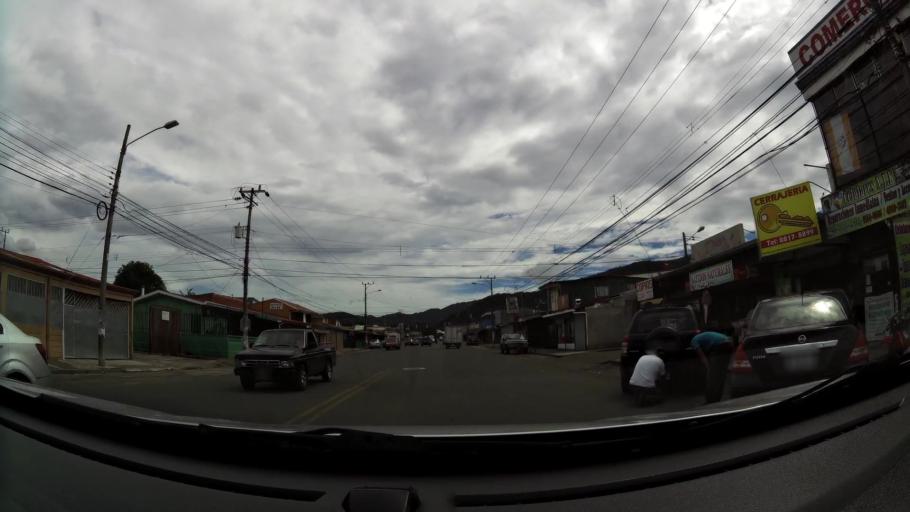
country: CR
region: San Jose
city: San Miguel
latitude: 9.8952
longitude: -84.0578
